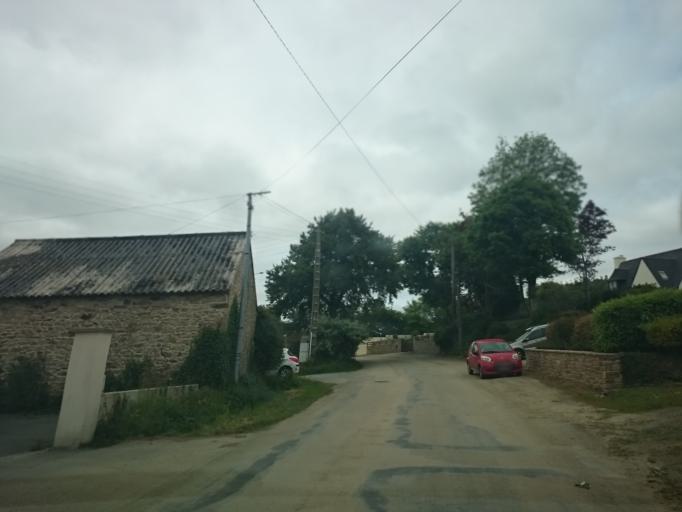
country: FR
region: Brittany
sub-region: Departement du Finistere
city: Gouesnou
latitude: 48.4540
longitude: -4.4525
